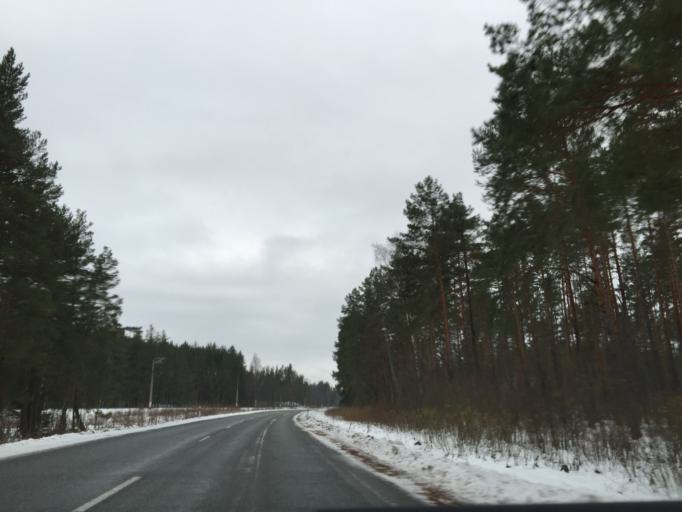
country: LV
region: Saulkrastu
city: Saulkrasti
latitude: 57.2085
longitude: 24.3804
